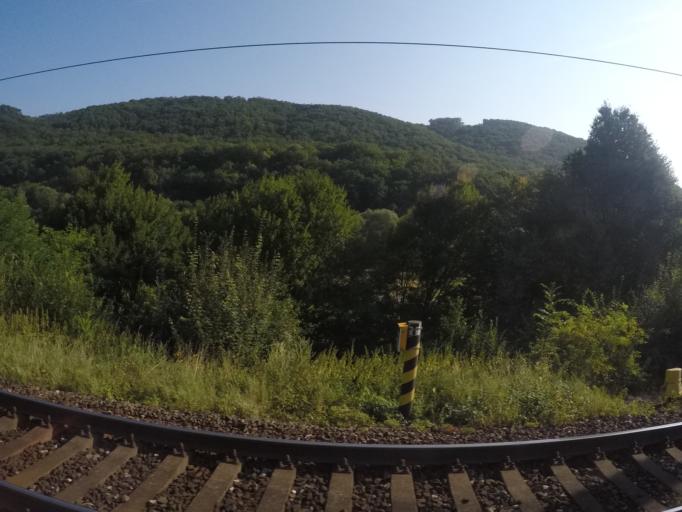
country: SK
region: Presovsky
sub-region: Okres Presov
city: Presov
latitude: 48.8628
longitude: 21.2103
